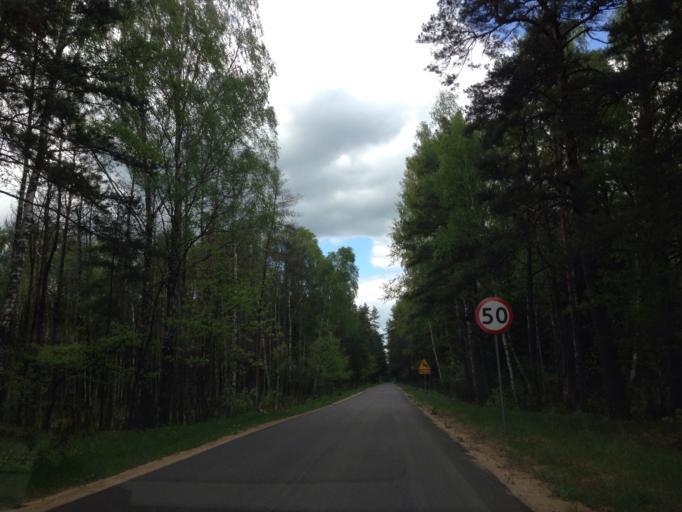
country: PL
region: Podlasie
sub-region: Powiat moniecki
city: Goniadz
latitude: 53.3517
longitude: 22.5981
